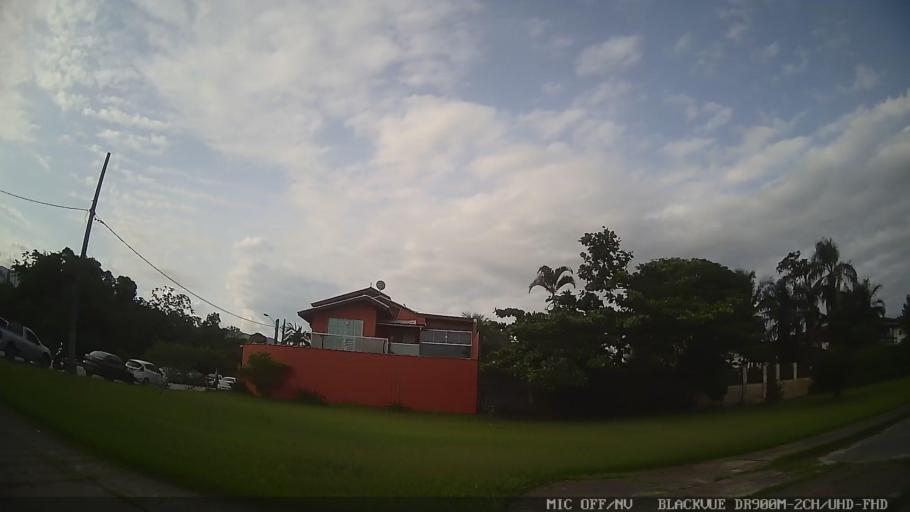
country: BR
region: Sao Paulo
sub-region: Bertioga
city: Bertioga
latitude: -23.8120
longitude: -46.0623
